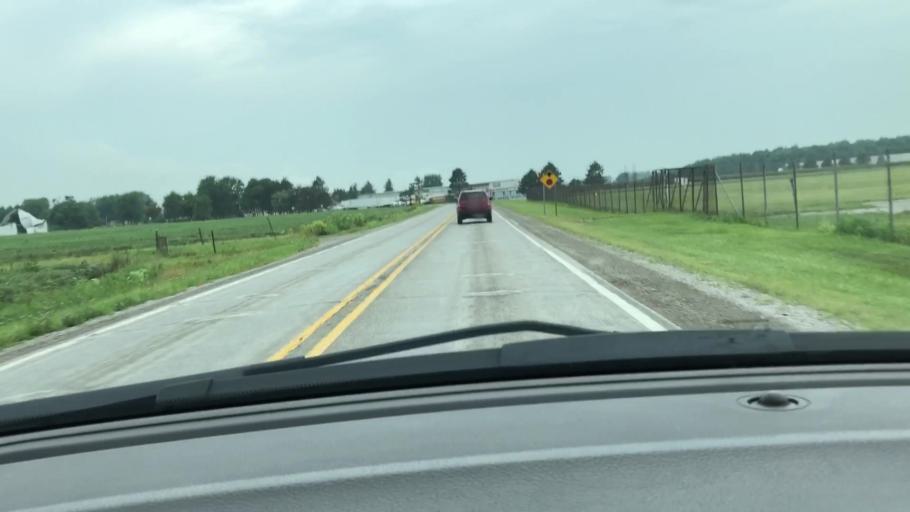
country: US
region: Michigan
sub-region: Saginaw County
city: Freeland
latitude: 43.5234
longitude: -84.0935
